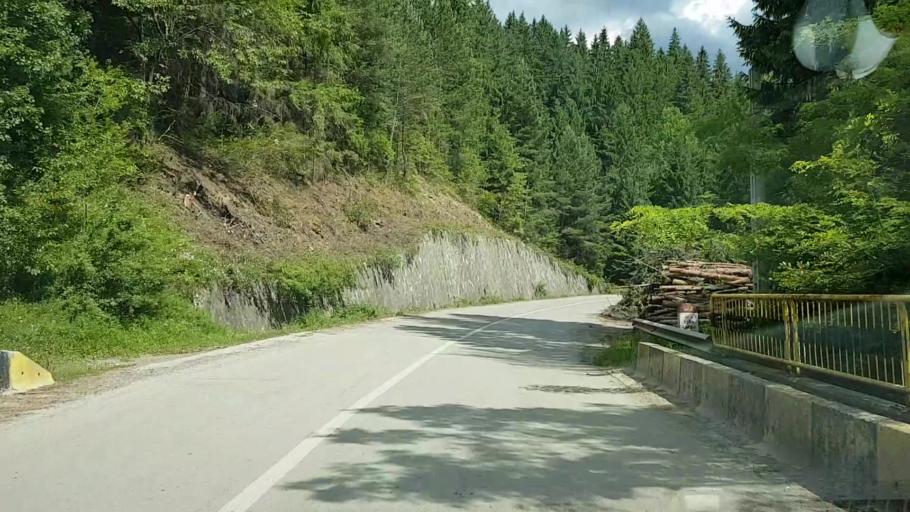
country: RO
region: Neamt
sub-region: Comuna Hangu
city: Hangu
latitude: 47.0529
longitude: 26.0042
